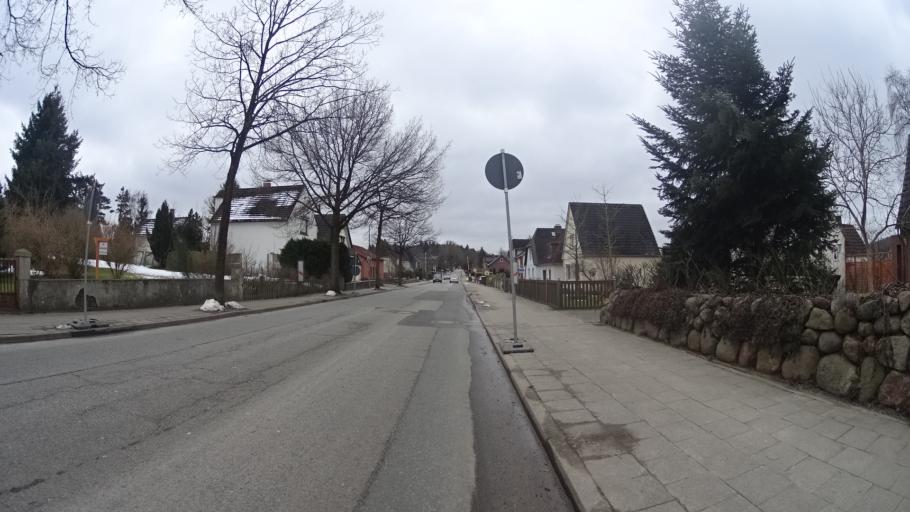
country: DE
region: Schleswig-Holstein
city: Malente
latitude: 54.1835
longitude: 10.5633
